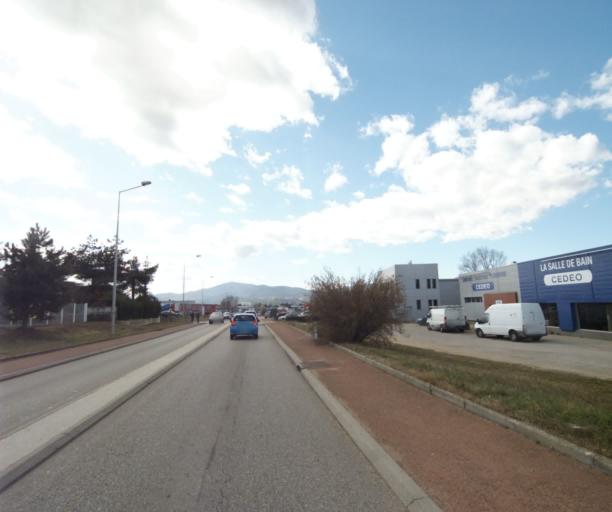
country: FR
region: Rhone-Alpes
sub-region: Departement de l'Ardeche
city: Davezieux
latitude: 45.2576
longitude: 4.6977
